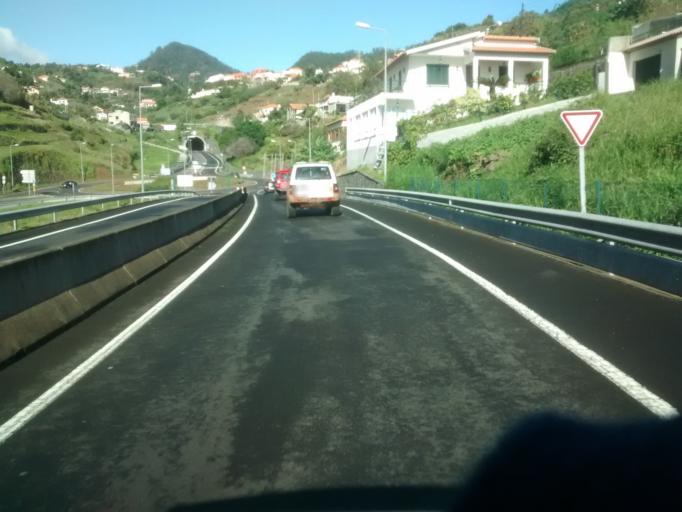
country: PT
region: Madeira
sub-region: Machico
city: Machico
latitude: 32.7297
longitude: -16.7797
